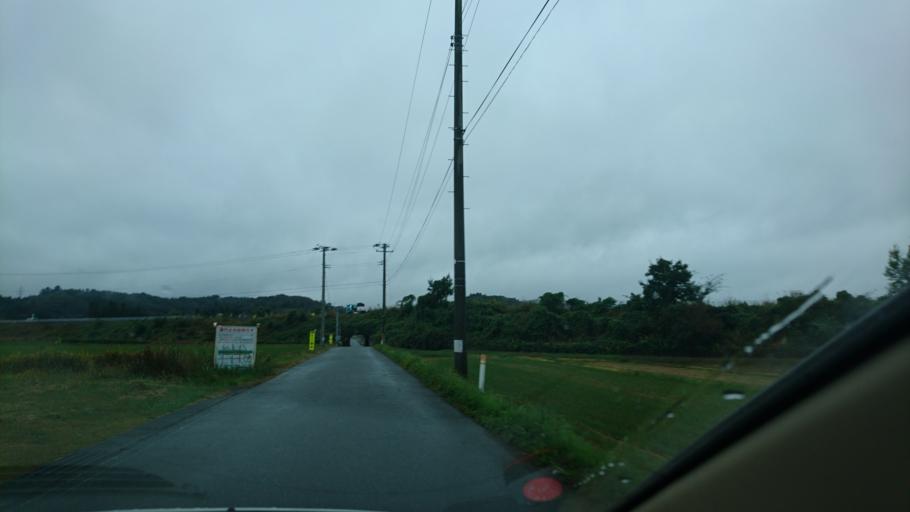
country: JP
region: Iwate
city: Ichinoseki
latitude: 38.9792
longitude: 141.1112
